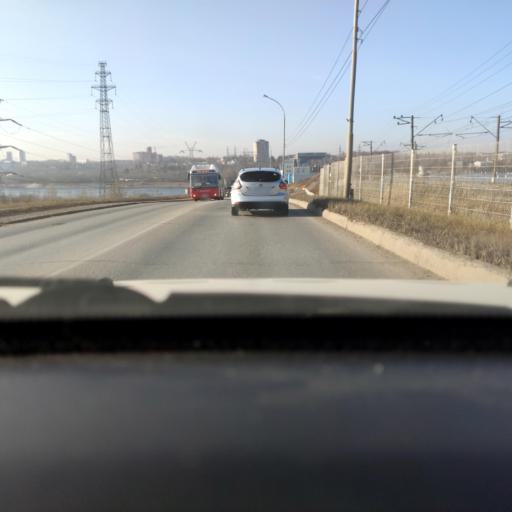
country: RU
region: Perm
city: Perm
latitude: 58.1146
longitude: 56.3412
